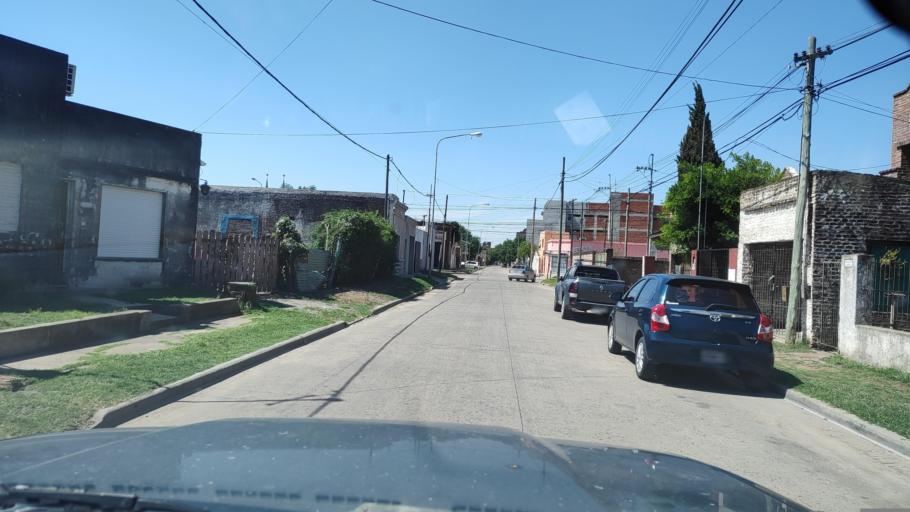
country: AR
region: Buenos Aires
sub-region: Partido de Lujan
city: Lujan
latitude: -34.5722
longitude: -59.1211
